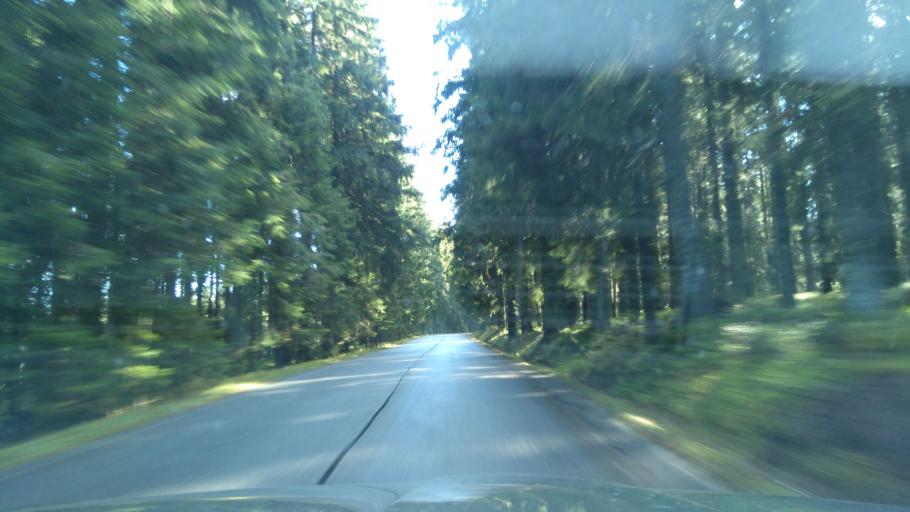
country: CZ
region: Jihocesky
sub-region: Okres Prachatice
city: Borova Lada
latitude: 49.0254
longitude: 13.5552
